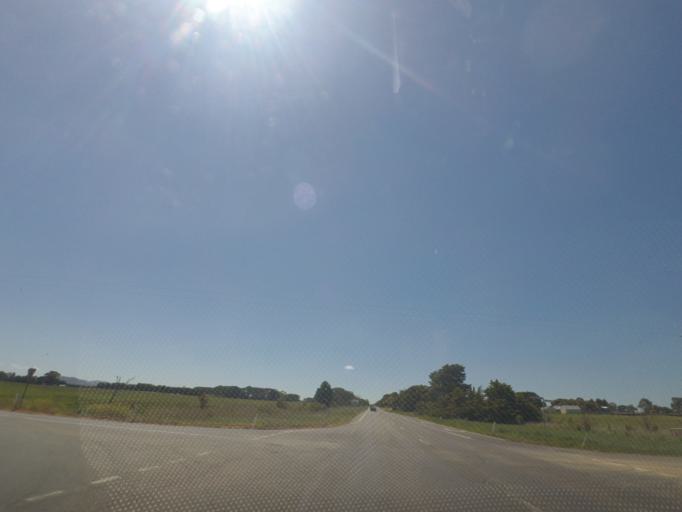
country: AU
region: Victoria
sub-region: Hume
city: Sunbury
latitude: -37.4534
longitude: 144.7429
